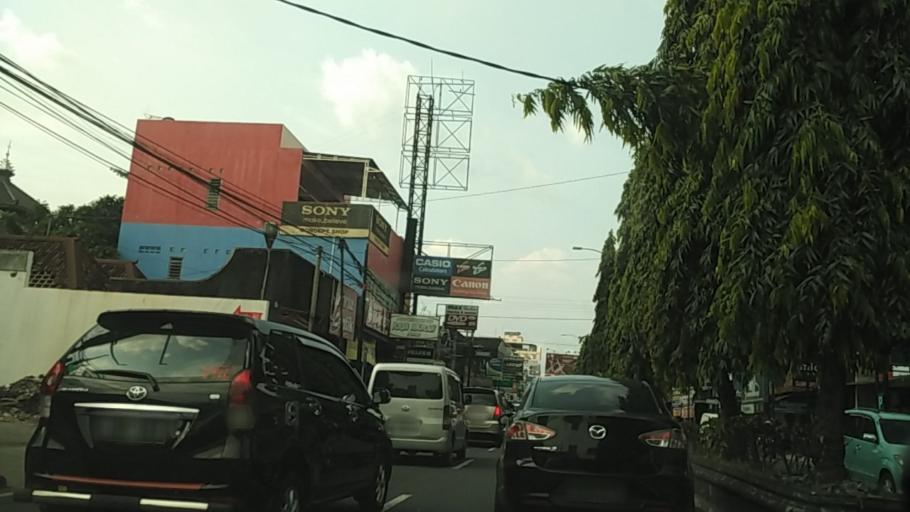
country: ID
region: Daerah Istimewa Yogyakarta
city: Yogyakarta
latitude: -7.7740
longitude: 110.3894
